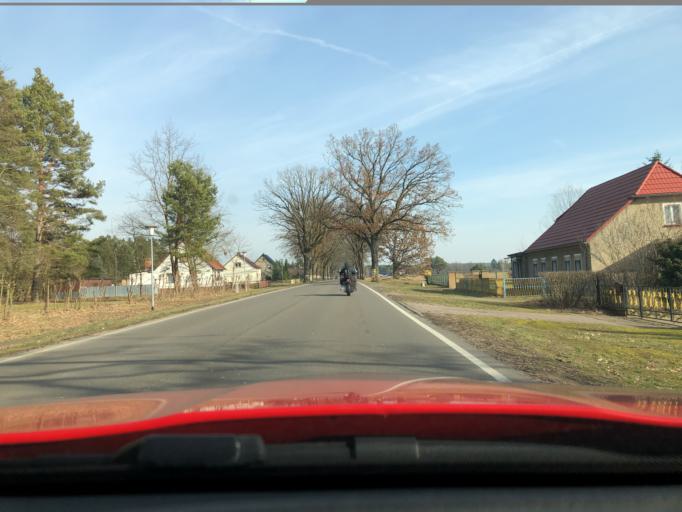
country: DE
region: Brandenburg
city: Waldsieversdorf
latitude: 52.4897
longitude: 14.0080
